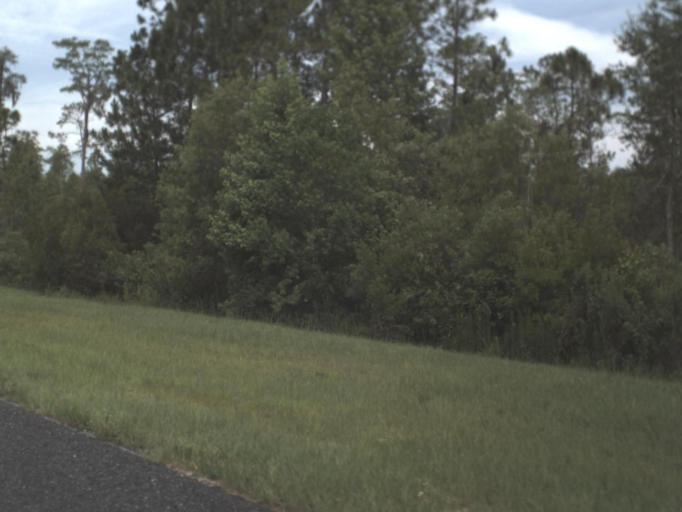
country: US
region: Florida
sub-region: Alachua County
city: Hawthorne
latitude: 29.6004
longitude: -82.1640
